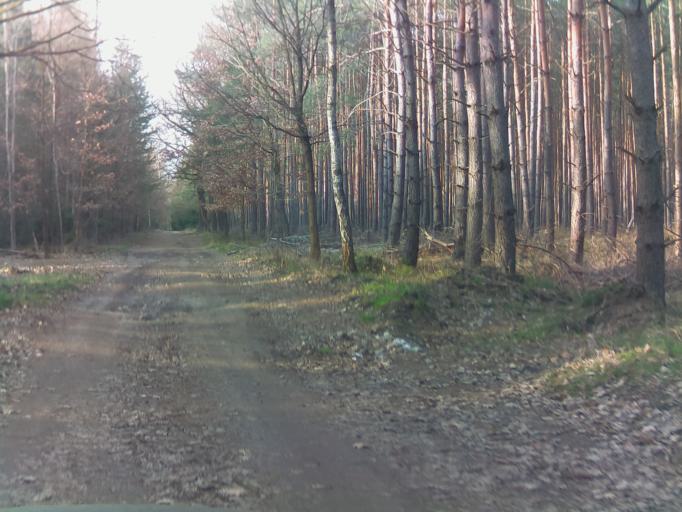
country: DE
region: Brandenburg
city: Schenkendobern
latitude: 51.9963
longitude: 14.5345
